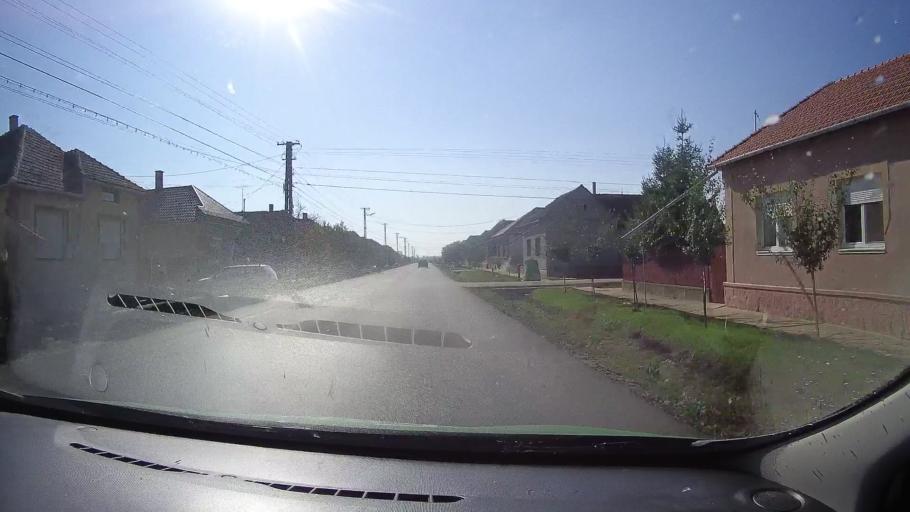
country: RO
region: Satu Mare
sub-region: Comuna Camin
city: Camin
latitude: 47.7251
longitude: 22.4761
